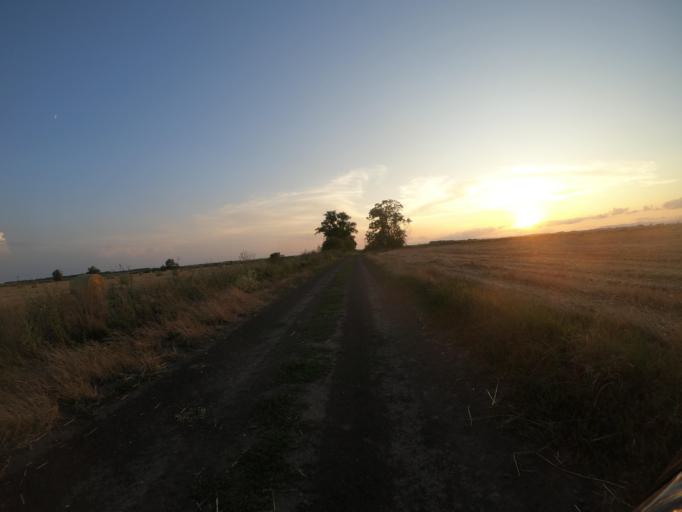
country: HU
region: Borsod-Abauj-Zemplen
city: Szentistvan
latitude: 47.7465
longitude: 20.7424
